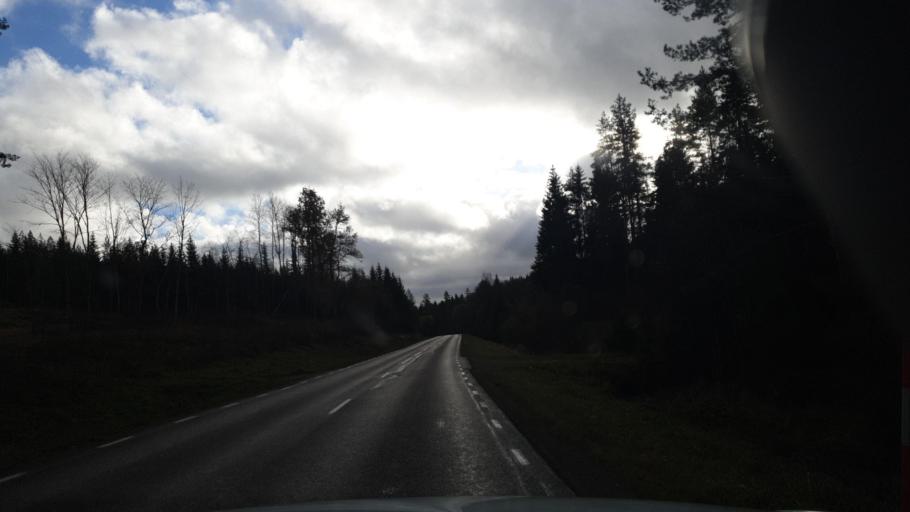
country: SE
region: Vaermland
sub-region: Grums Kommun
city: Slottsbron
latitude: 59.4573
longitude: 12.8362
